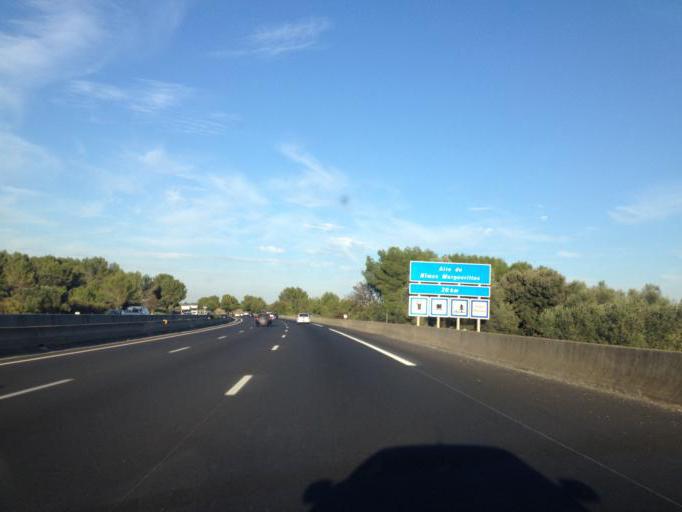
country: FR
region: Languedoc-Roussillon
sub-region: Departement du Gard
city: Vergeze
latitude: 43.7486
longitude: 4.2400
